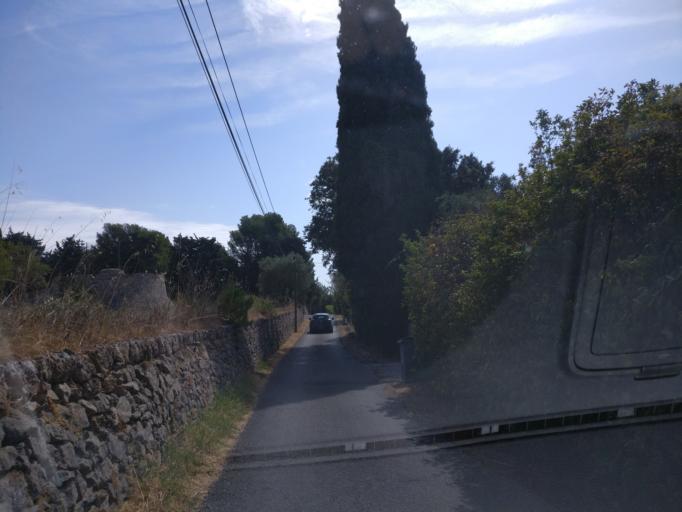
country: FR
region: Provence-Alpes-Cote d'Azur
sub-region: Departement du Var
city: Sanary-sur-Mer
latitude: 43.1370
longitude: 5.8163
